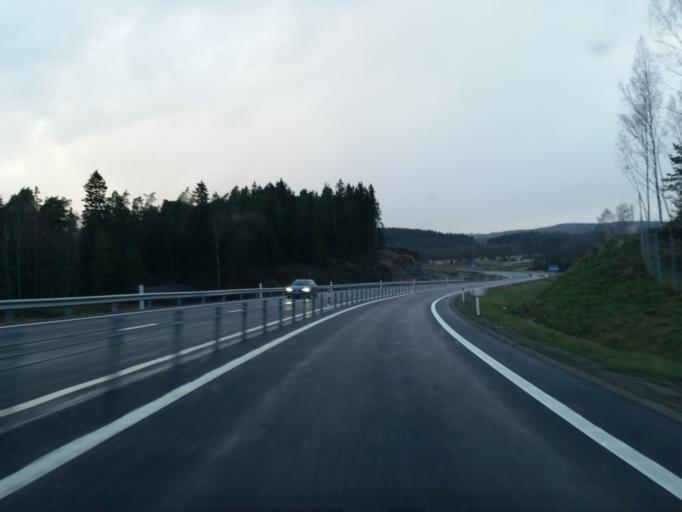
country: SE
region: Vaestra Goetaland
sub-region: Boras Kommun
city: Boras
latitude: 57.6904
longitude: 12.9201
